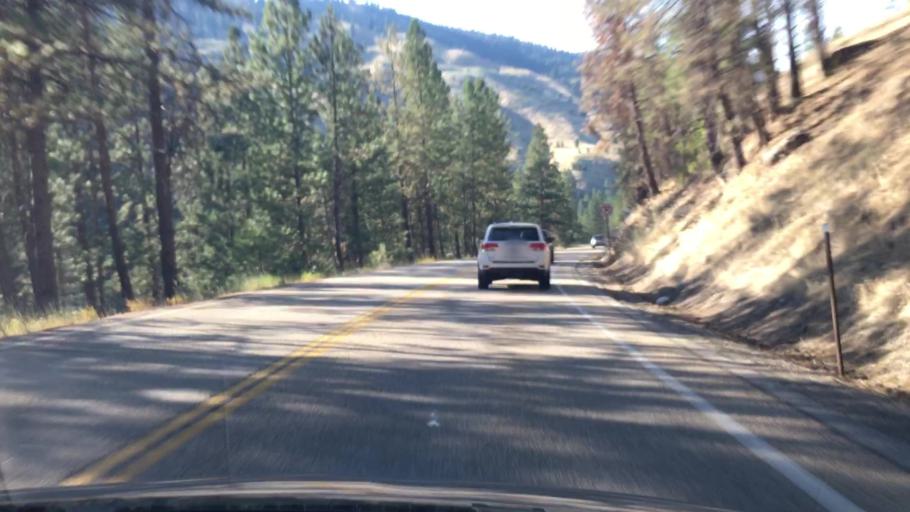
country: US
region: Idaho
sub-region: Boise County
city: Idaho City
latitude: 44.0747
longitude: -116.1200
